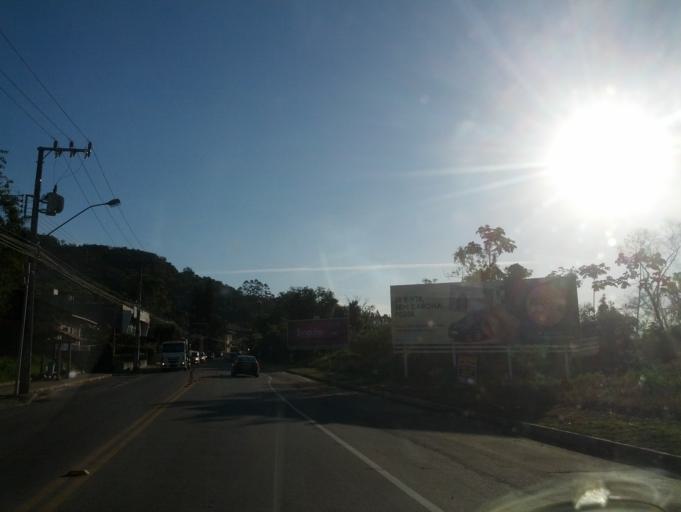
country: BR
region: Santa Catarina
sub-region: Indaial
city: Indaial
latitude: -26.8903
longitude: -49.1959
